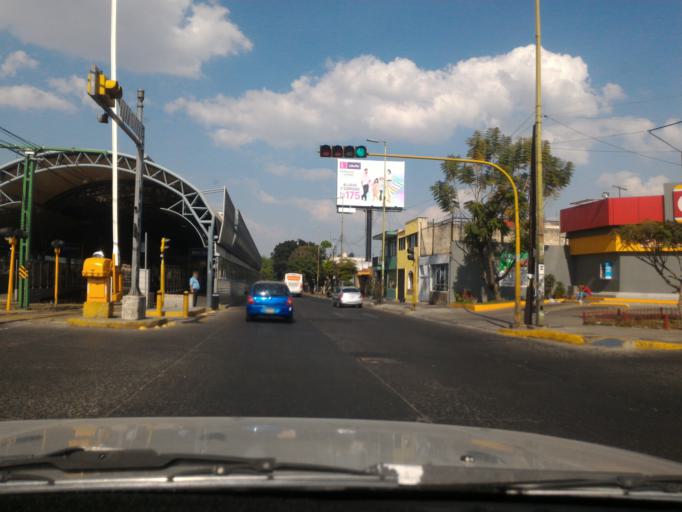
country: MX
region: Jalisco
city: Guadalajara
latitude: 20.6424
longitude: -103.3733
